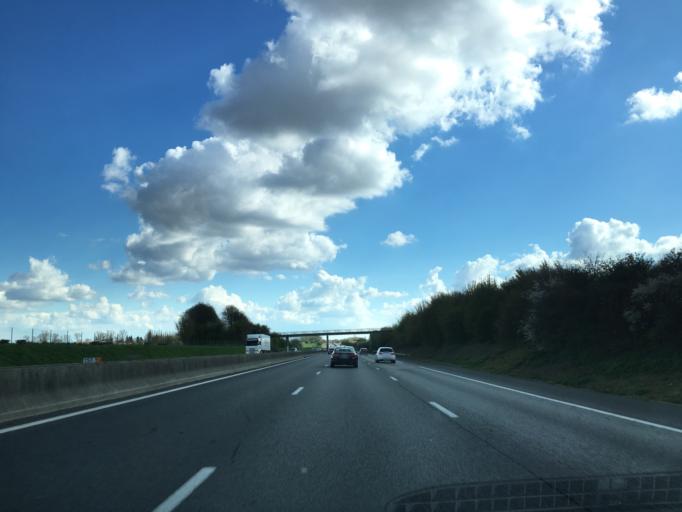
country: FR
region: Nord-Pas-de-Calais
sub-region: Departement du Pas-de-Calais
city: Vaulx-Vraucourt
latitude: 50.1397
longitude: 2.8720
